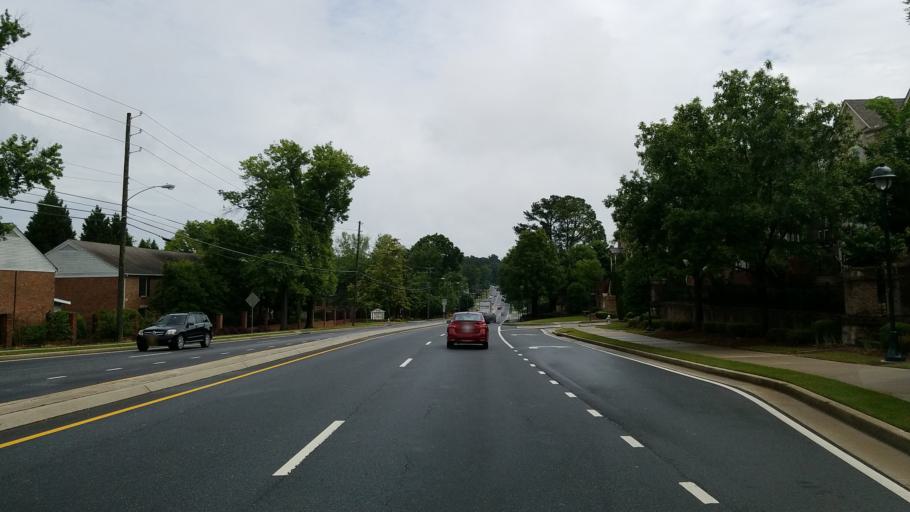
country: US
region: Georgia
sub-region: Fulton County
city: Sandy Springs
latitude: 33.9382
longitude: -84.3772
